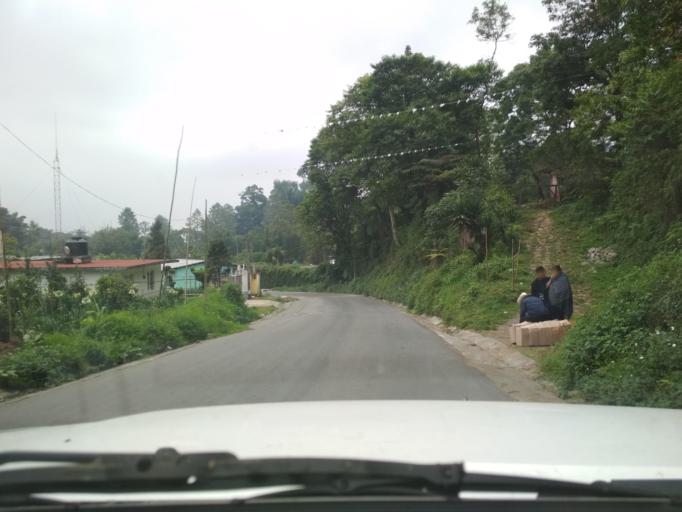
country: MX
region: Veracruz
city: La Perla
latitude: 18.9341
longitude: -97.1425
